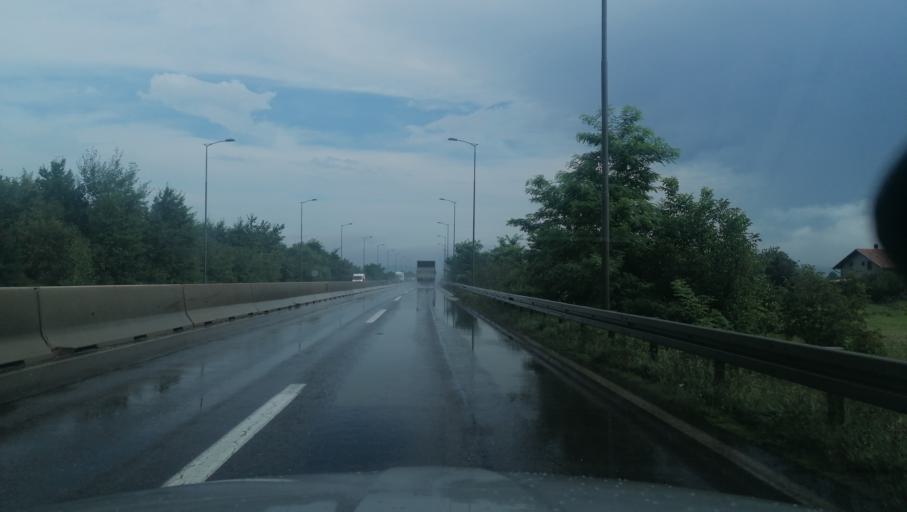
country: BA
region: Republika Srpska
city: Trn
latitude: 44.8324
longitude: 17.2127
